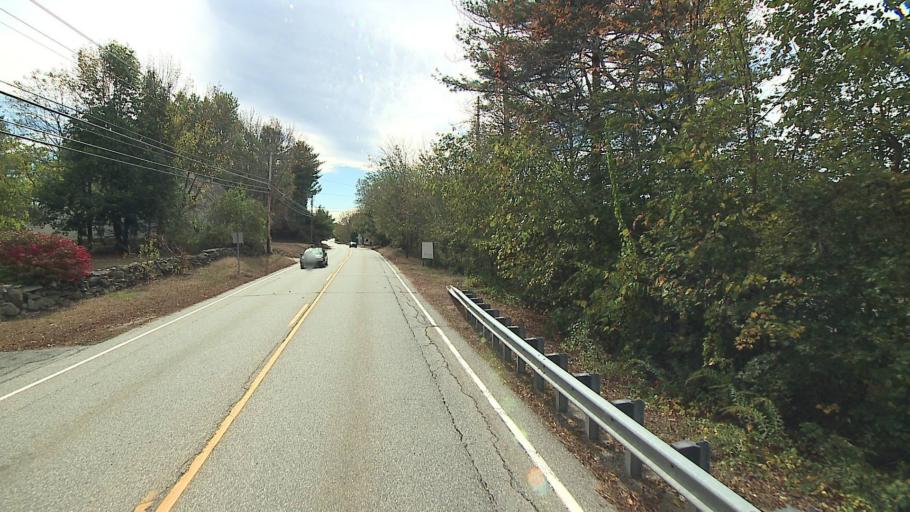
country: US
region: Connecticut
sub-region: Windham County
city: Killingly Center
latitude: 41.8700
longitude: -71.8798
